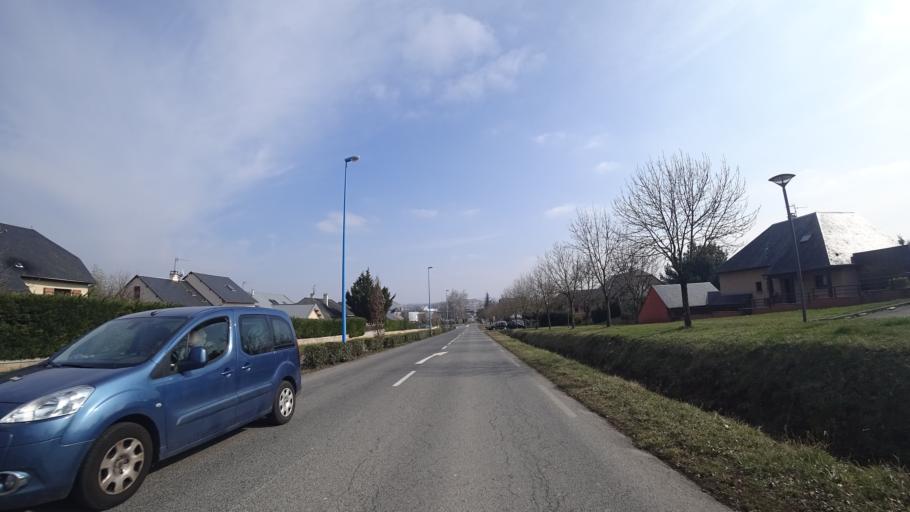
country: FR
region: Midi-Pyrenees
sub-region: Departement de l'Aveyron
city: Rodez
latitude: 44.3734
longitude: 2.5753
